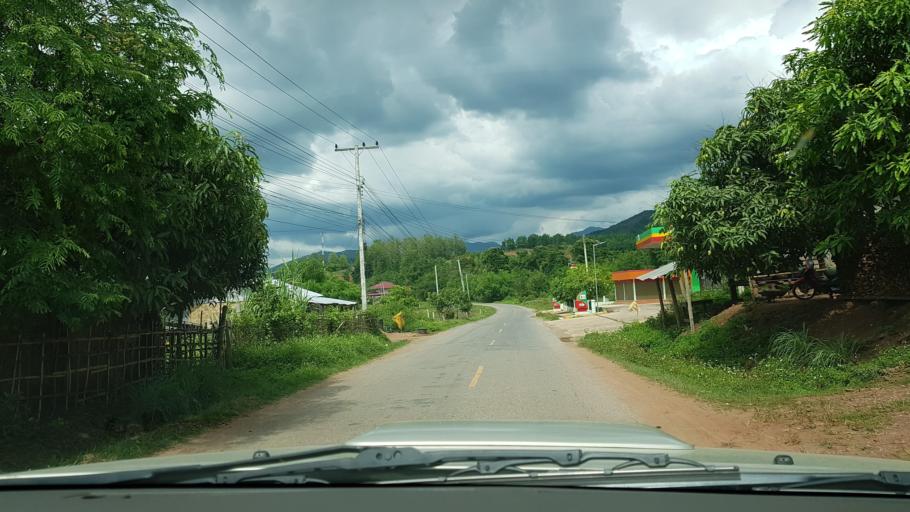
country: LA
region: Loungnamtha
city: Muang Nale
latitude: 20.2891
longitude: 101.6294
